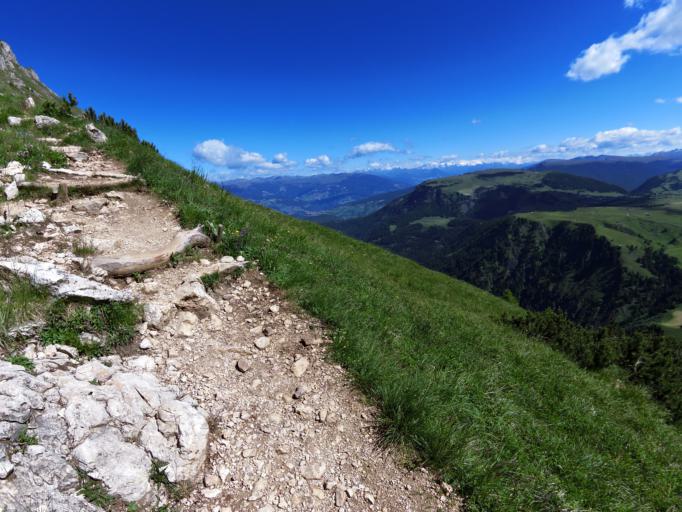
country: IT
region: Trentino-Alto Adige
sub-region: Bolzano
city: Siusi
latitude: 46.5116
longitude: 11.5883
